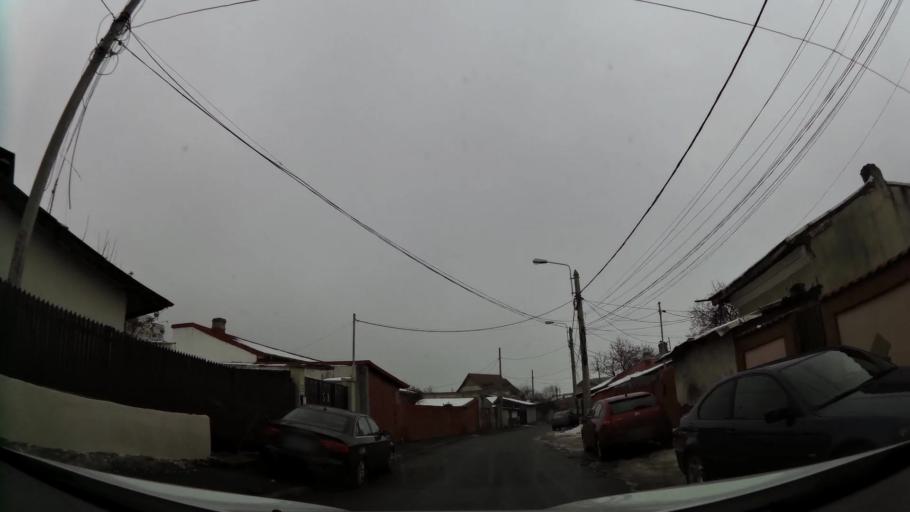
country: RO
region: Ilfov
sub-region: Comuna Popesti-Leordeni
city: Popesti-Leordeni
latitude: 44.4087
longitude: 26.1621
